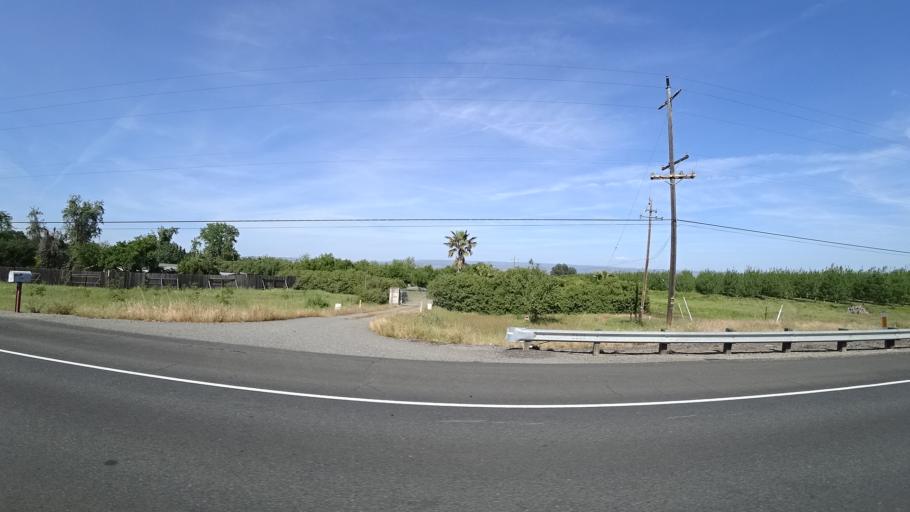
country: US
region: California
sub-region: Glenn County
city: Hamilton City
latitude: 39.8794
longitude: -121.9715
